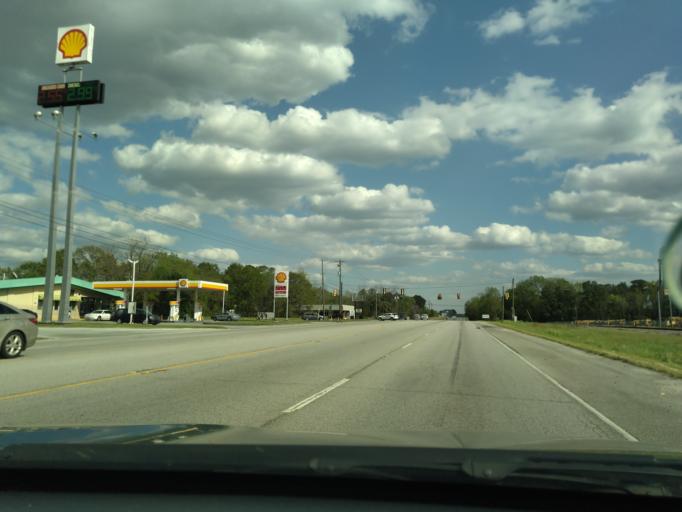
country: US
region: South Carolina
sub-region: Florence County
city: Florence
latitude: 34.2227
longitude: -79.7908
